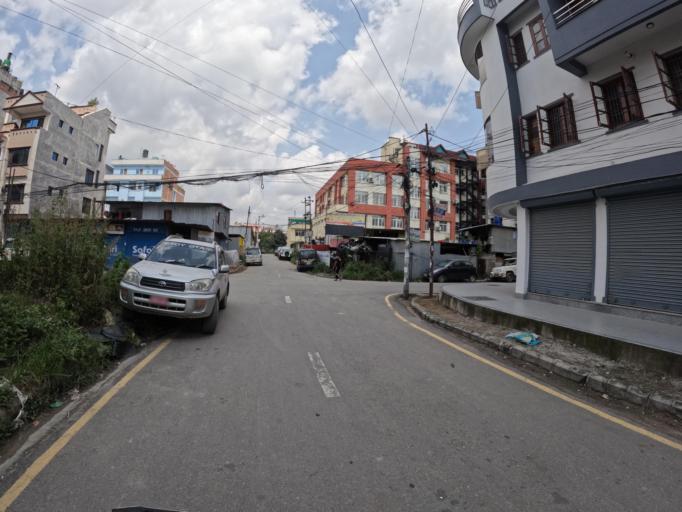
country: NP
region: Central Region
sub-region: Bagmati Zone
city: Patan
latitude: 27.6700
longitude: 85.3534
